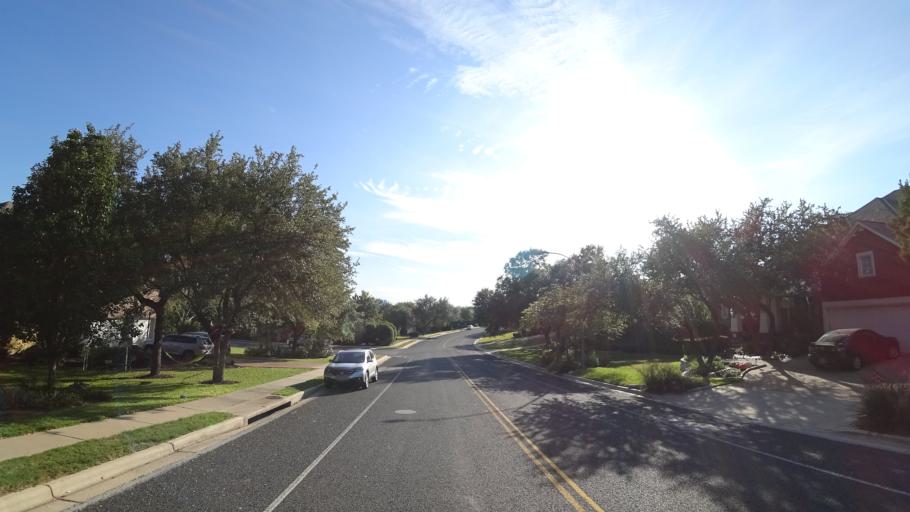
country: US
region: Texas
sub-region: Williamson County
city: Anderson Mill
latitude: 30.4293
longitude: -97.8084
